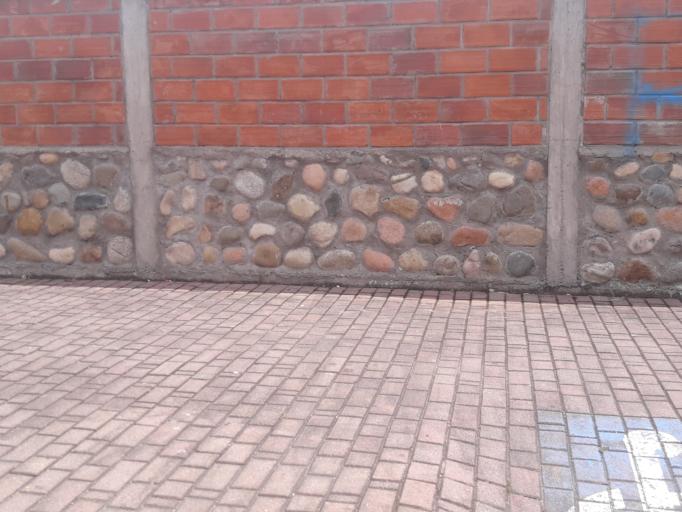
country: EC
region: Napo
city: Tena
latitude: -0.9916
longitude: -77.8139
